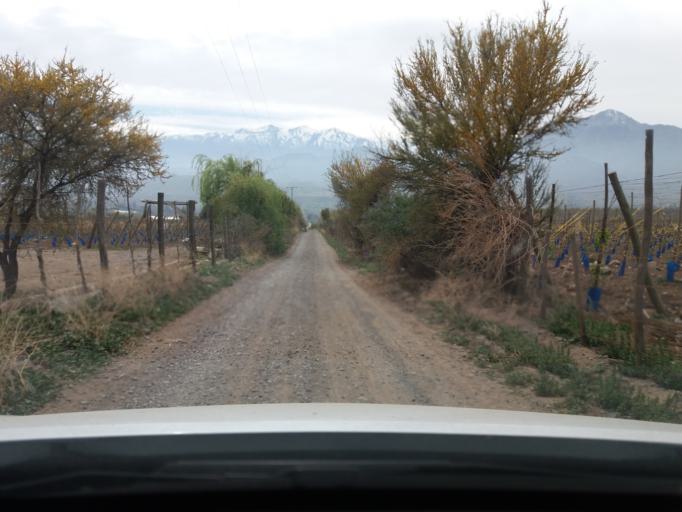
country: CL
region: Valparaiso
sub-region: Provincia de Los Andes
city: Los Andes
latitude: -32.8505
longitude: -70.5567
